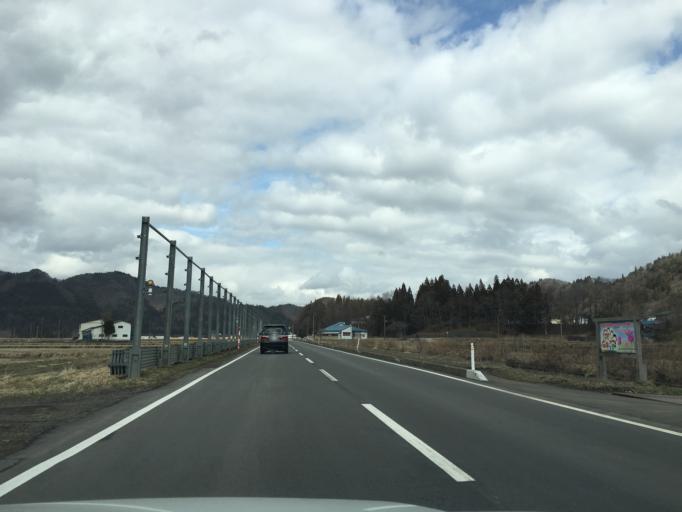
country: JP
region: Akita
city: Hanawa
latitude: 40.2336
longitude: 140.7344
